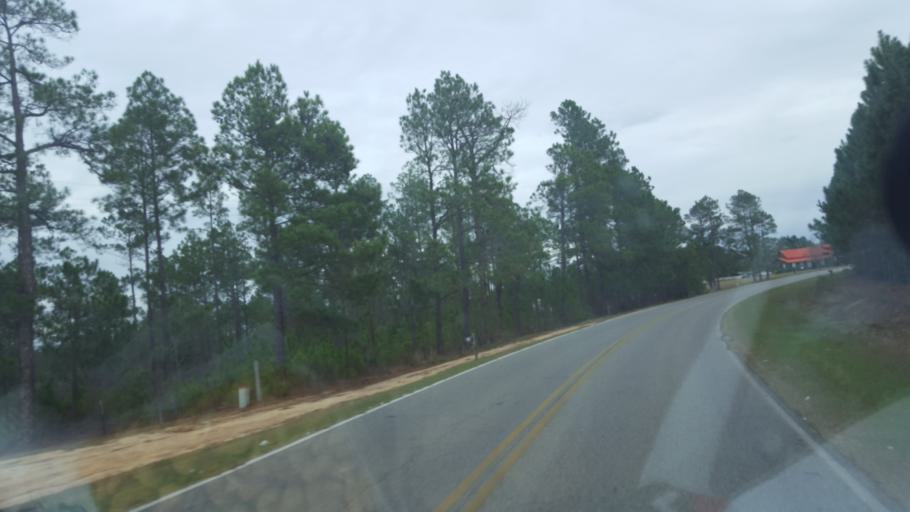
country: US
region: Georgia
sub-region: Ben Hill County
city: Fitzgerald
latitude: 31.7562
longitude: -83.3396
